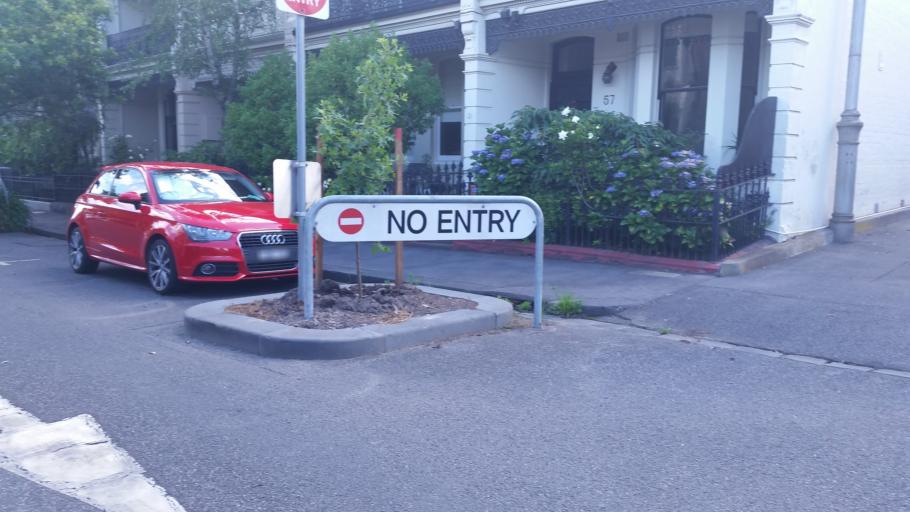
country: AU
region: Victoria
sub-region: Melbourne
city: East Melbourne
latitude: -37.8178
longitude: 144.9887
